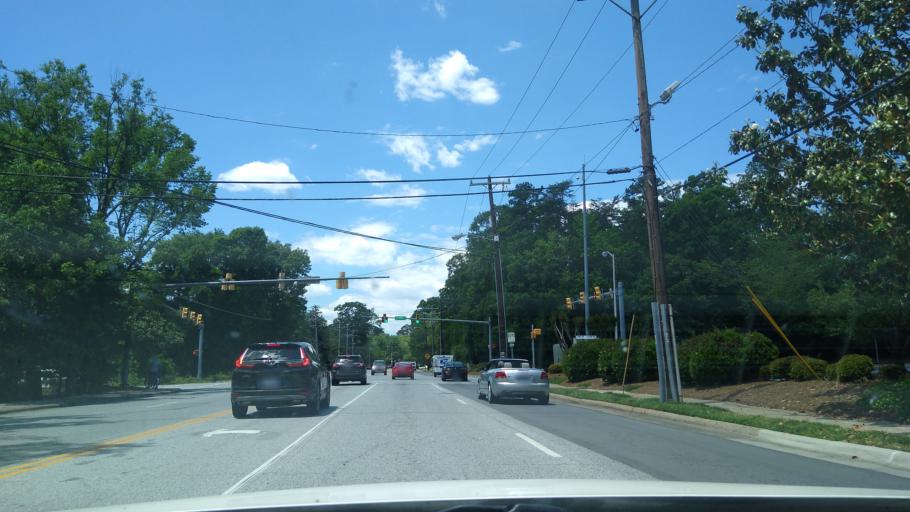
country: US
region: North Carolina
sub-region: Guilford County
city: Greensboro
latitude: 36.0873
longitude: -79.8447
